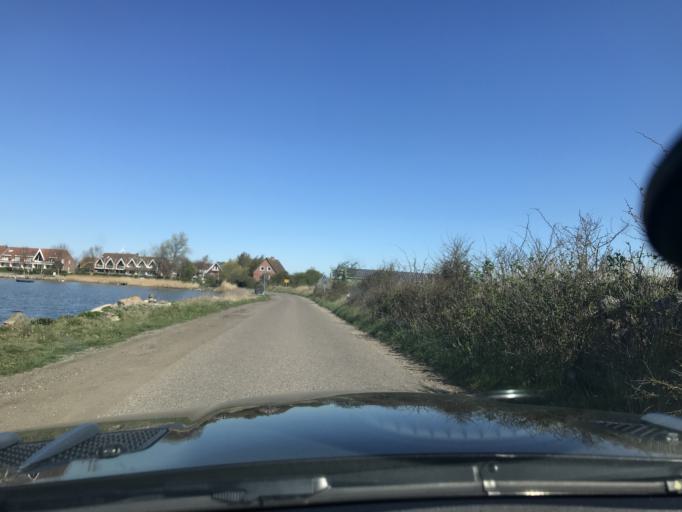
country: DE
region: Schleswig-Holstein
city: Grossenbrode
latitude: 54.4450
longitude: 11.0958
